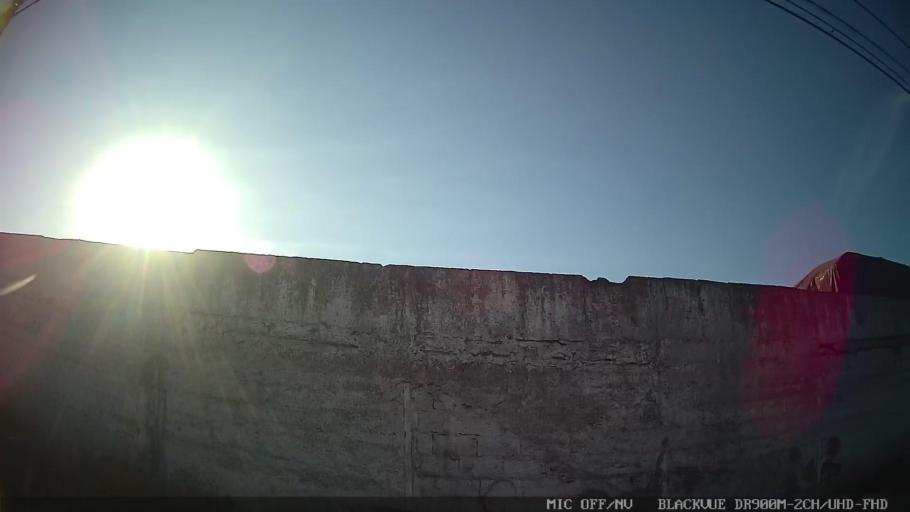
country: BR
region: Sao Paulo
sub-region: Guaruja
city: Guaruja
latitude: -23.9633
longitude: -46.2783
